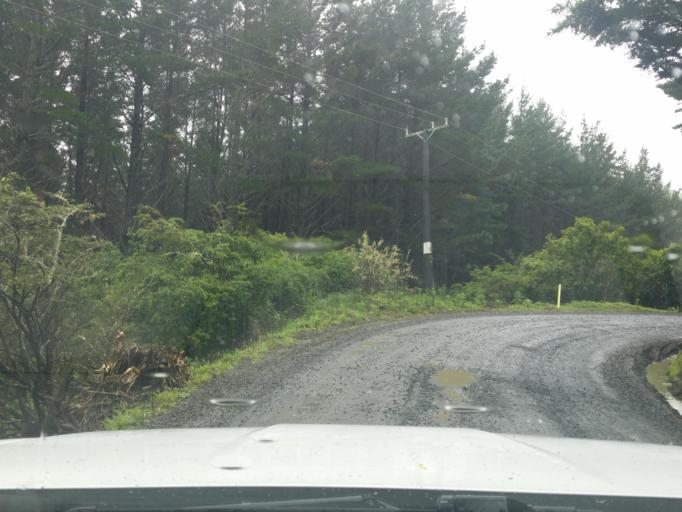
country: NZ
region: Northland
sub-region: Kaipara District
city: Dargaville
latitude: -35.7827
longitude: 173.9883
